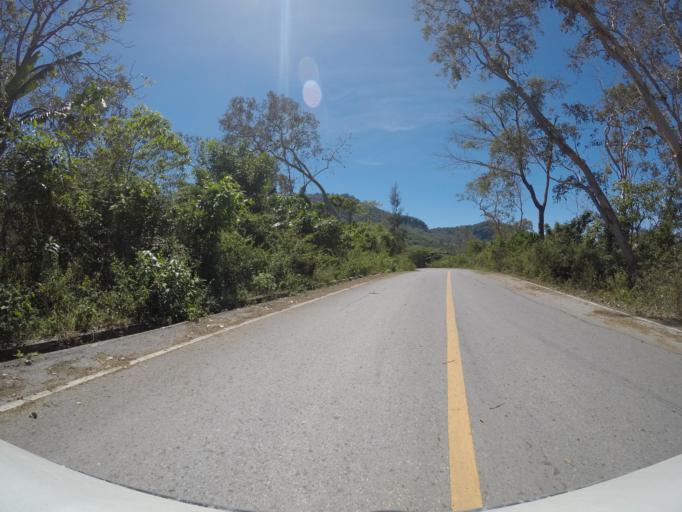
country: TL
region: Manatuto
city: Manatuto
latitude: -8.8132
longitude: 125.9727
